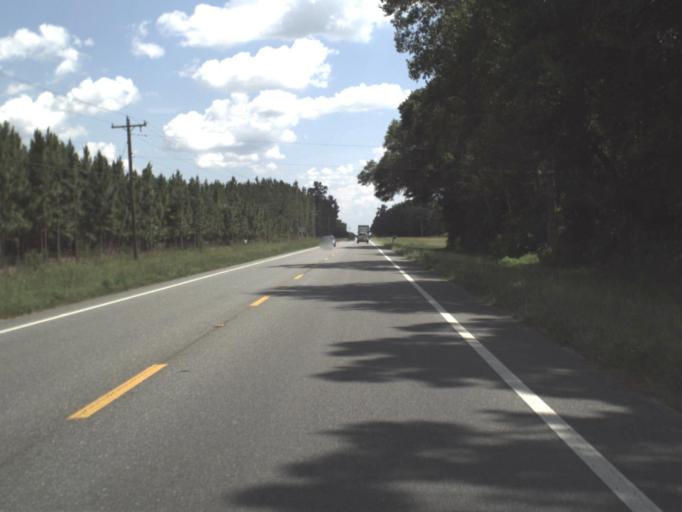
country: US
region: Florida
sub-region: Columbia County
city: Watertown
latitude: 30.0596
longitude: -82.5995
